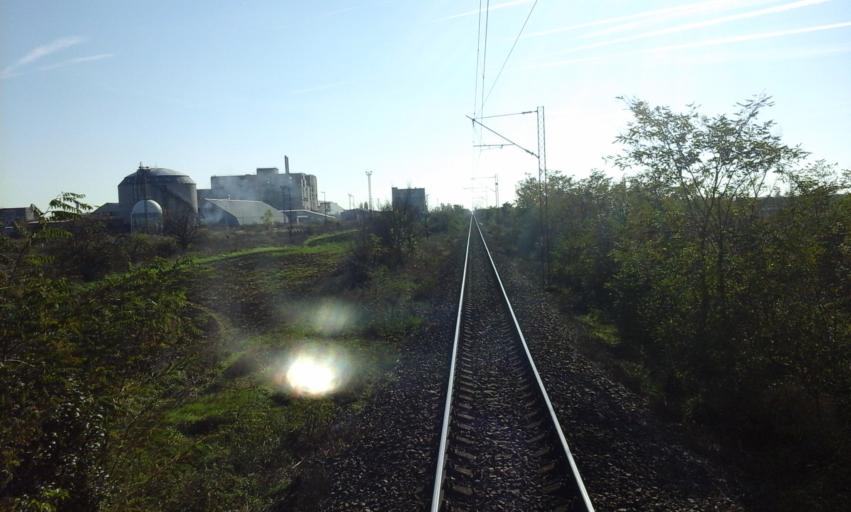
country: RS
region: Autonomna Pokrajina Vojvodina
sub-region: Severnobacki Okrug
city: Subotica
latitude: 46.0113
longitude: 19.6793
